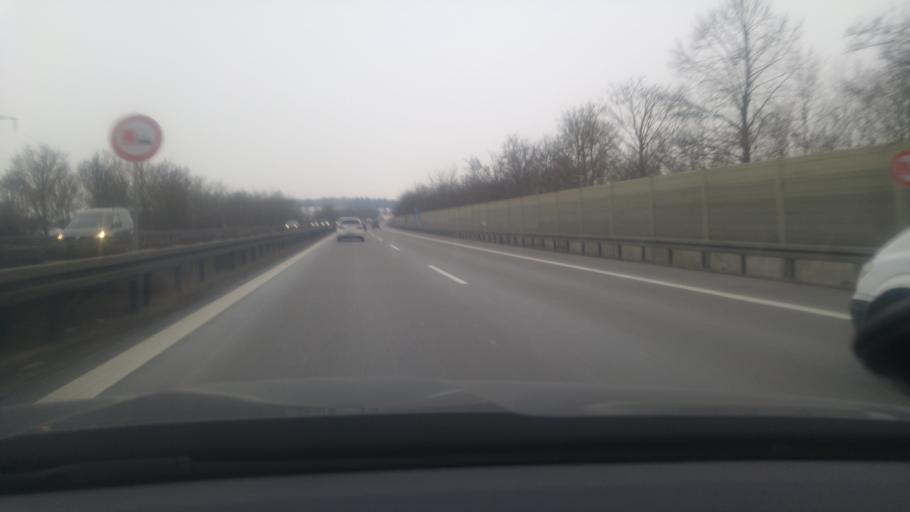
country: DE
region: Baden-Wuerttemberg
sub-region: Regierungsbezirk Stuttgart
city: Motzingen
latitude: 48.4641
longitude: 8.7831
